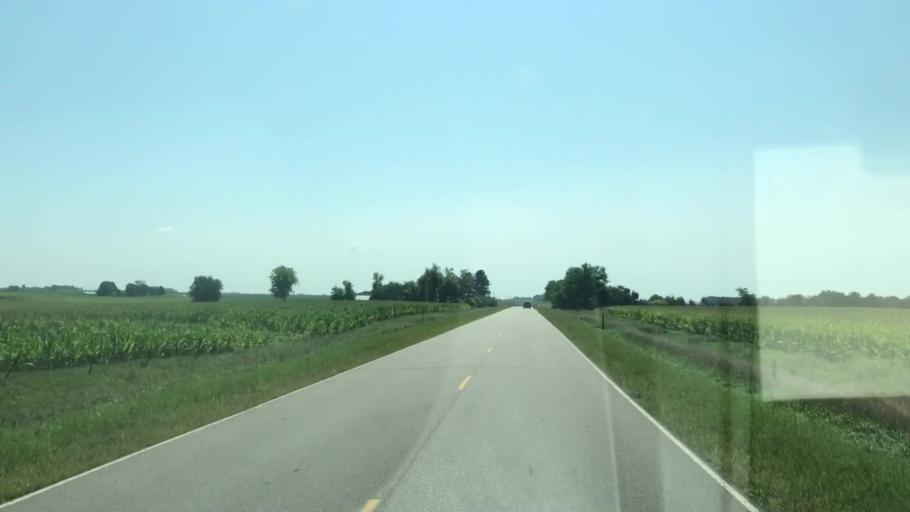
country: US
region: Iowa
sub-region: O'Brien County
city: Sanborn
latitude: 43.1929
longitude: -95.7230
